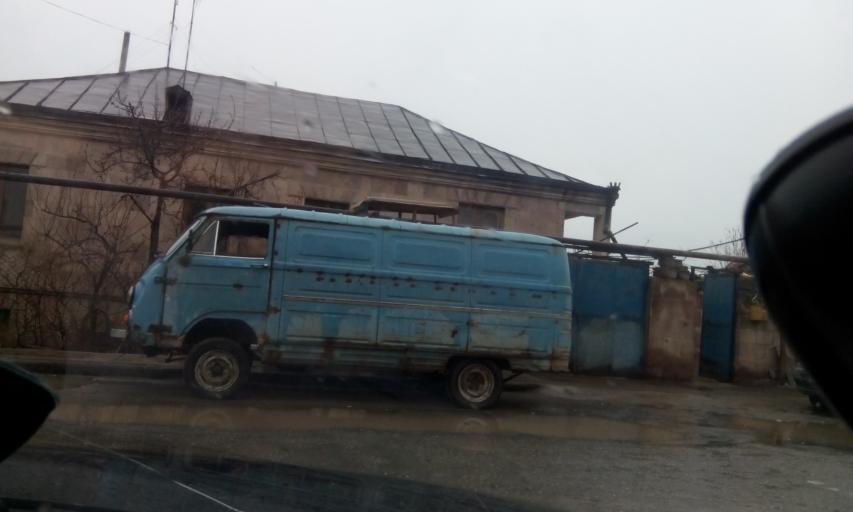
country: AM
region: Armavir
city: Pshatavan
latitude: 40.0356
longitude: 44.0626
